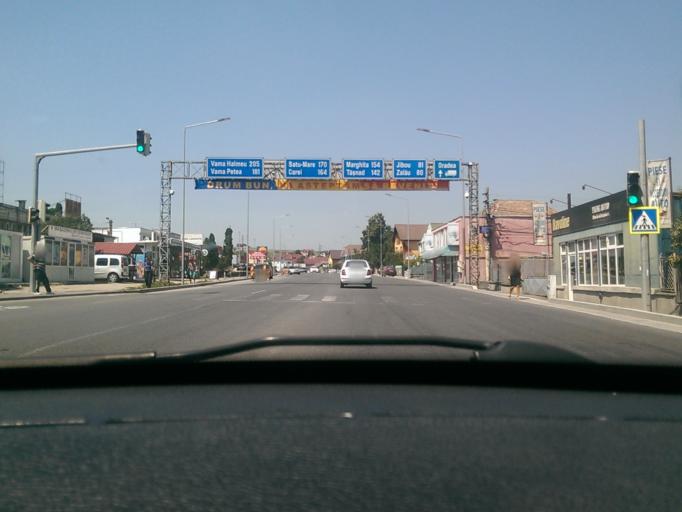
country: RO
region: Cluj
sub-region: Comuna Baciu
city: Baciu
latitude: 46.7846
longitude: 23.5554
